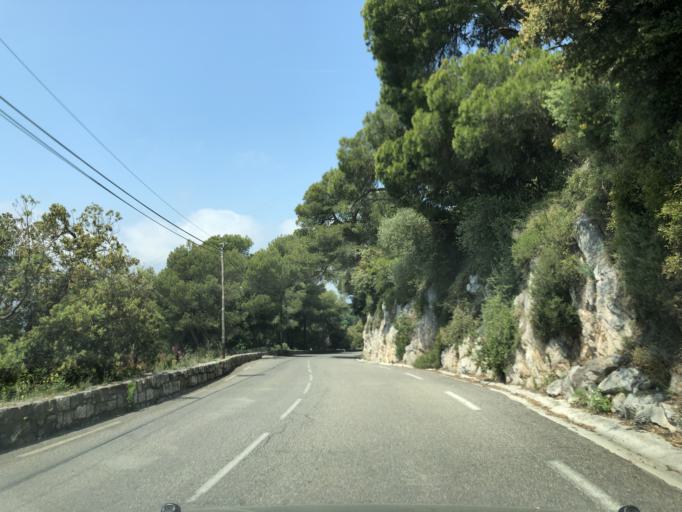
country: FR
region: Provence-Alpes-Cote d'Azur
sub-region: Departement des Alpes-Maritimes
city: Beaulieu-sur-Mer
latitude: 43.7168
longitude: 7.3197
